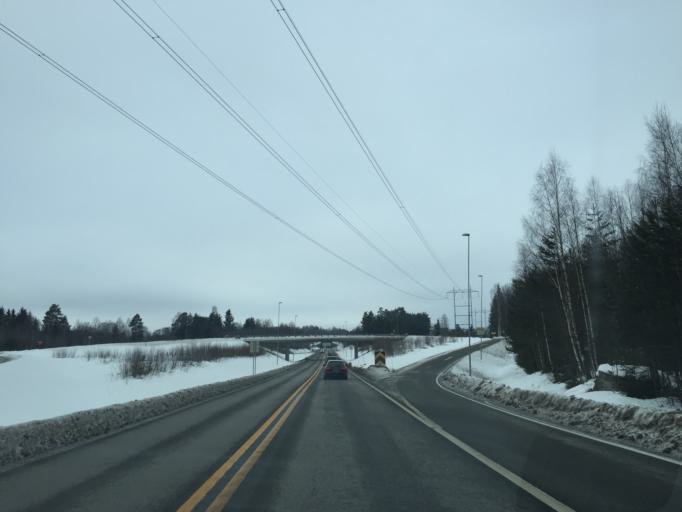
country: NO
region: Hedmark
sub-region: Loten
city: Loten
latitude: 60.7855
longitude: 11.3041
